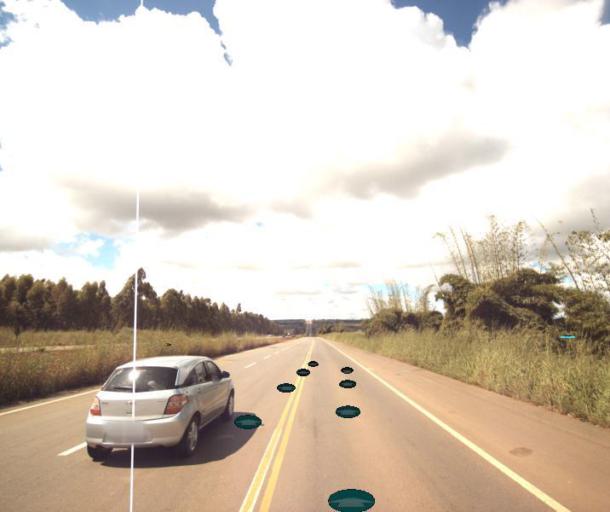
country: BR
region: Goias
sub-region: Anapolis
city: Anapolis
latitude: -16.1991
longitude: -49.0244
